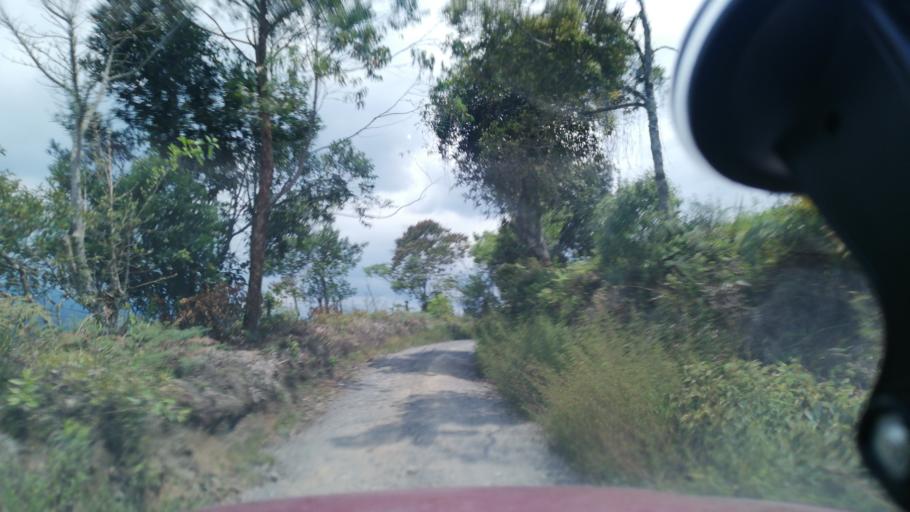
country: CO
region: Cundinamarca
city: Vergara
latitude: 5.1923
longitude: -74.2743
